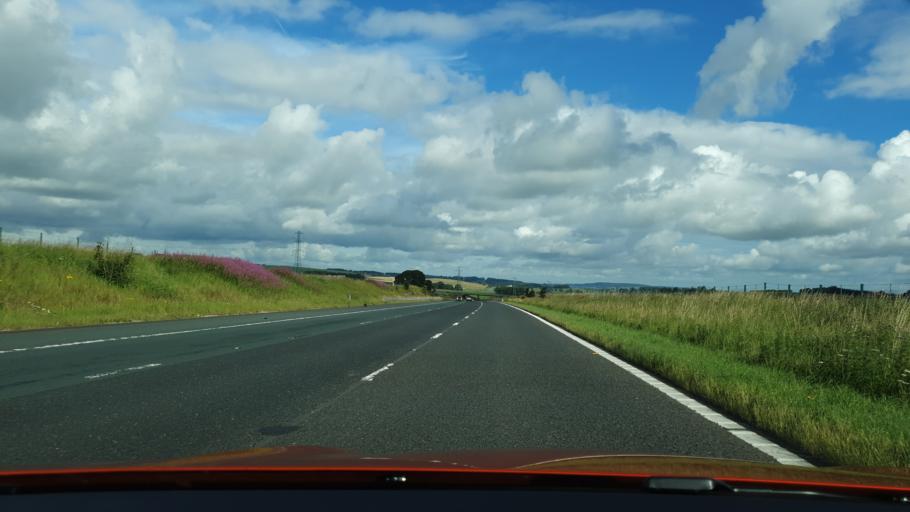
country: GB
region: England
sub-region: Cumbria
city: Penrith
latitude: 54.5417
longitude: -2.6646
